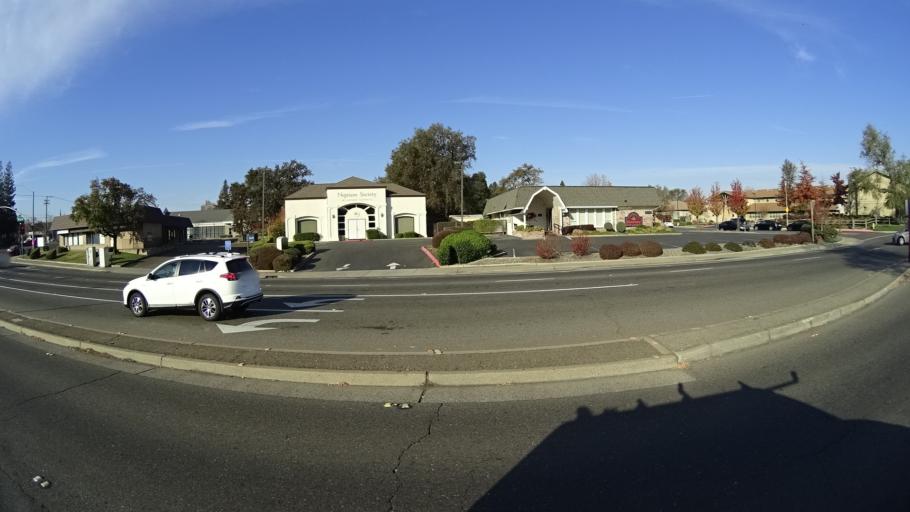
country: US
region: California
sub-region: Sacramento County
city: Foothill Farms
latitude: 38.6613
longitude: -121.3368
